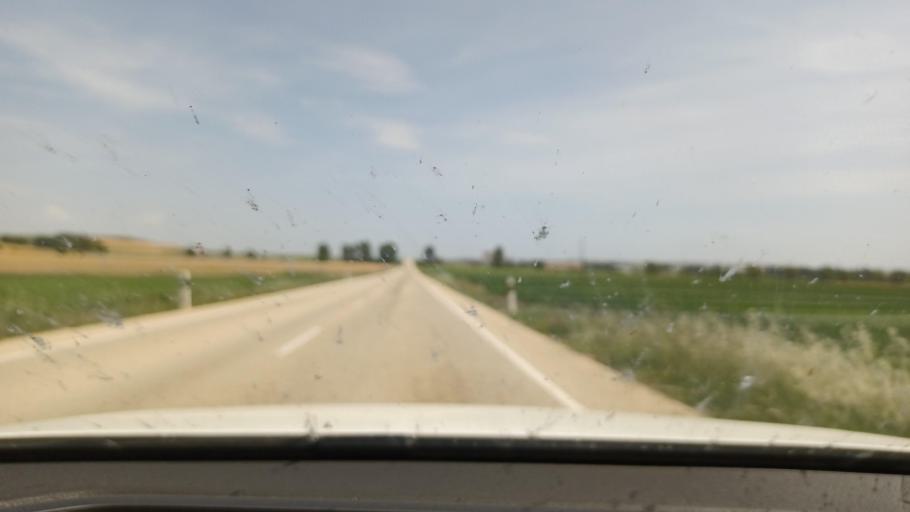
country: ES
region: Castille and Leon
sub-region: Provincia de Soria
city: Coscurita
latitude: 41.4531
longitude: -2.4840
